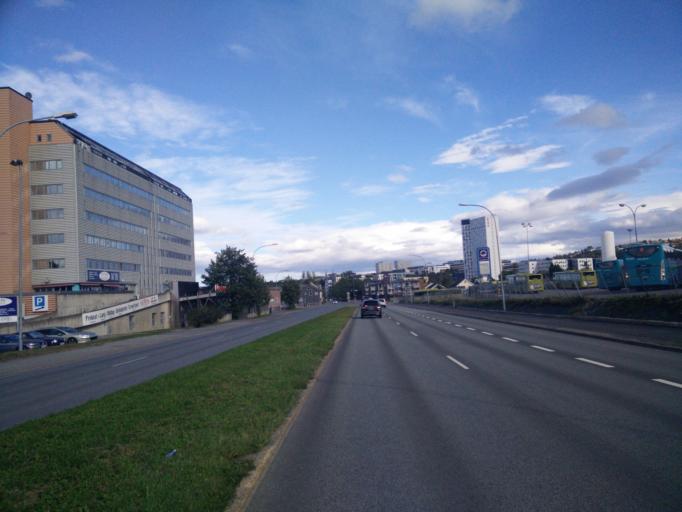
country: NO
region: Sor-Trondelag
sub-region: Trondheim
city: Trondheim
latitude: 63.4067
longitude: 10.3978
